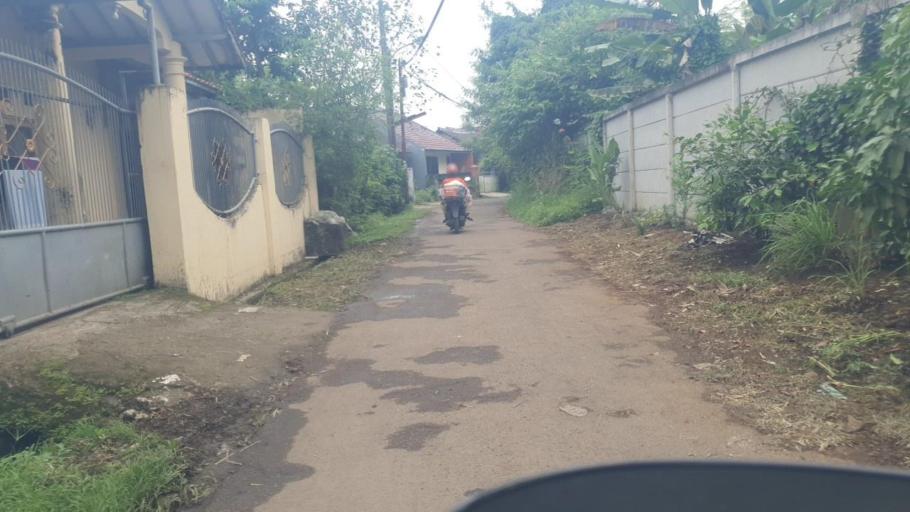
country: ID
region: West Java
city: Bogor
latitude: -6.5798
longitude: 106.7840
